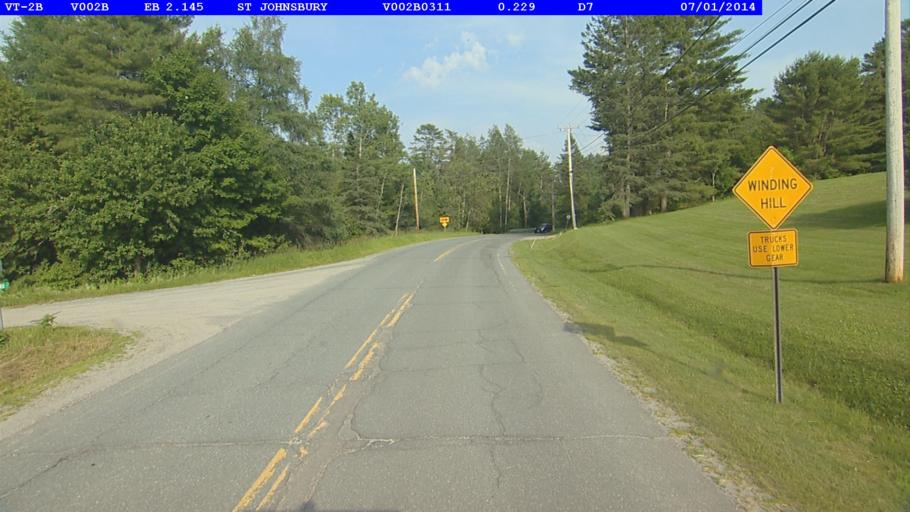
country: US
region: Vermont
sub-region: Caledonia County
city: St Johnsbury
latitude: 44.4282
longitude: -72.0517
